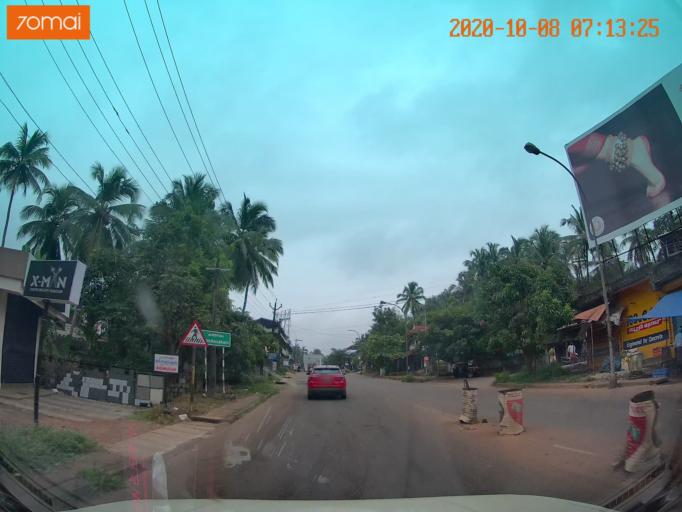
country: IN
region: Kerala
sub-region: Malappuram
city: Ponnani
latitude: 10.8117
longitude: 76.0110
